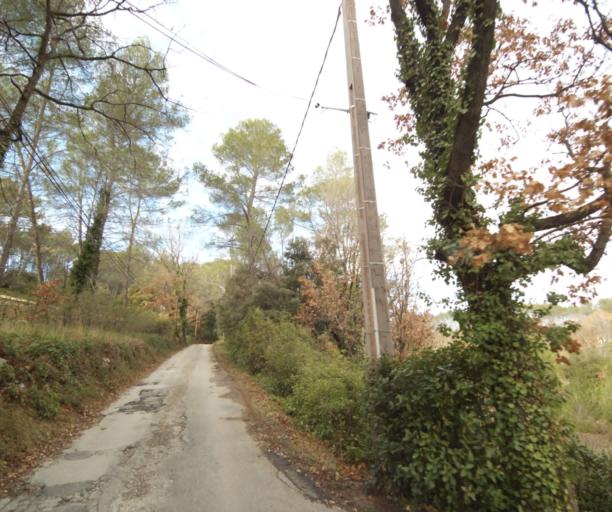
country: FR
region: Provence-Alpes-Cote d'Azur
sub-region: Departement du Var
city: Trans-en-Provence
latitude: 43.5123
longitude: 6.4964
